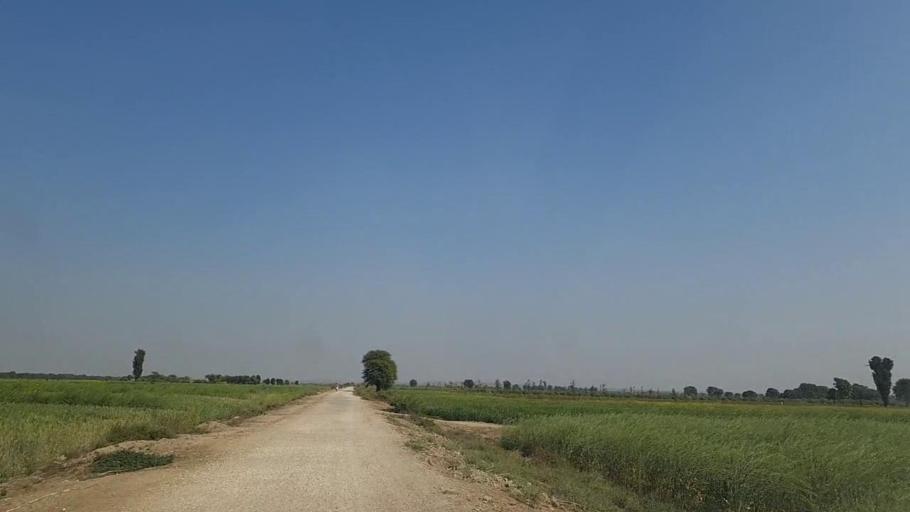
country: PK
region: Sindh
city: Naukot
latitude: 24.8991
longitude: 69.4613
